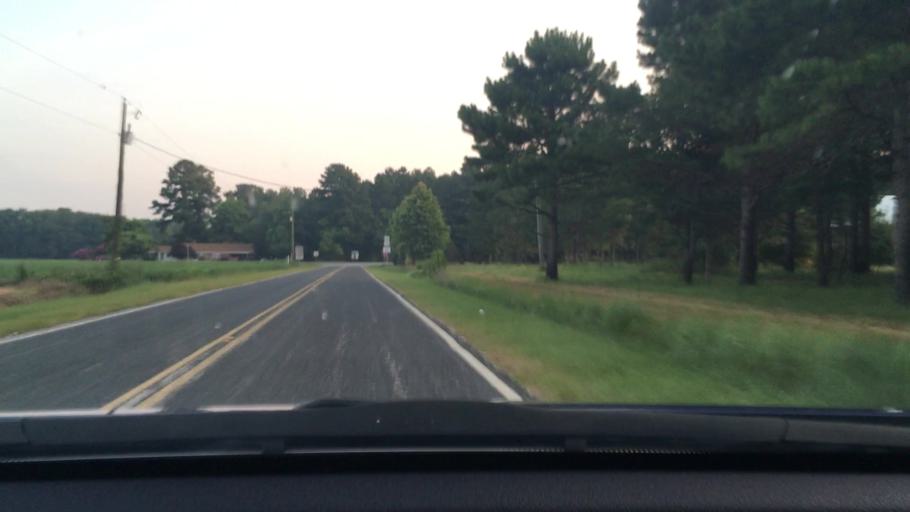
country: US
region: South Carolina
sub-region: Lee County
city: Bishopville
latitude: 34.2667
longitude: -80.1377
